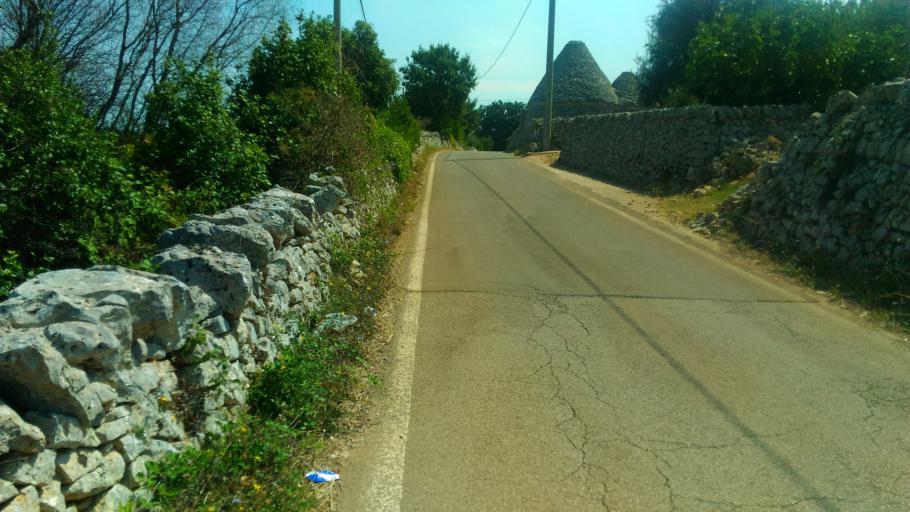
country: IT
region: Apulia
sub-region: Provincia di Bari
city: Locorotondo
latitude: 40.7519
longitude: 17.3539
